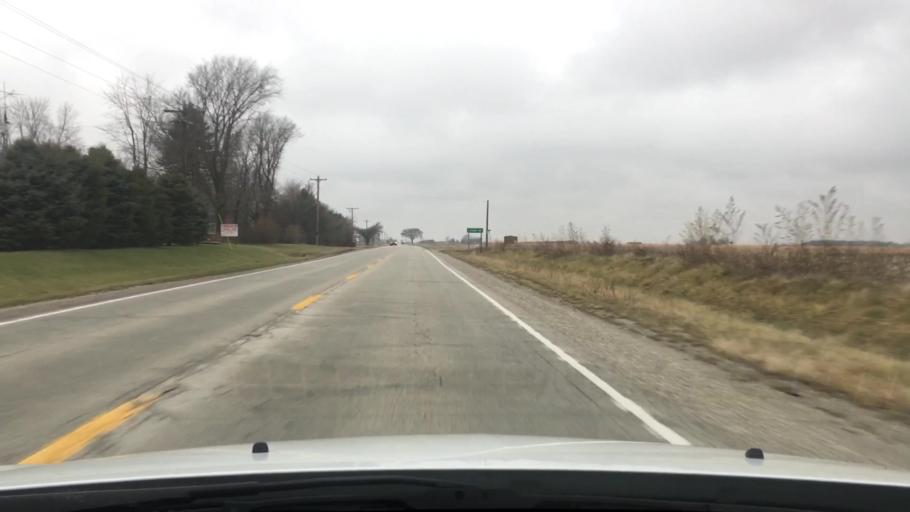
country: US
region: Illinois
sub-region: Iroquois County
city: Clifton
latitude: 40.8876
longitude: -87.8453
